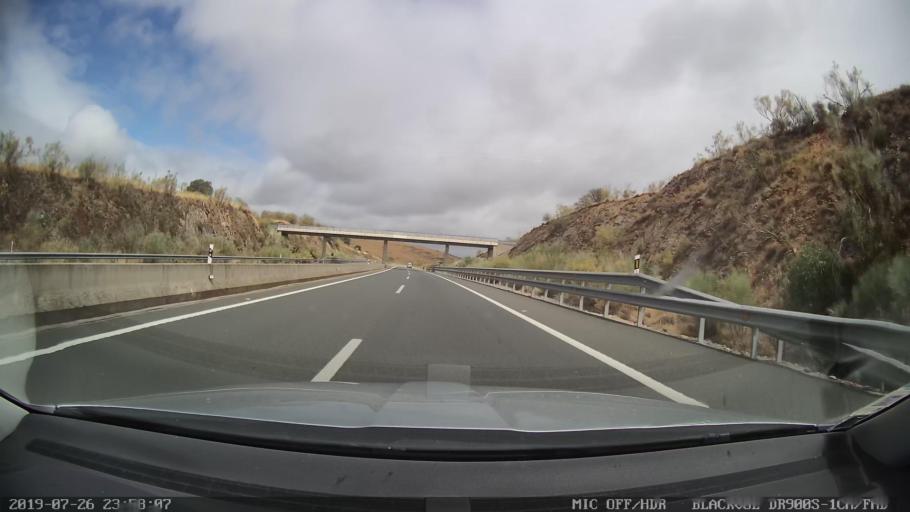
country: ES
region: Extremadura
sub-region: Provincia de Caceres
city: Romangordo
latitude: 39.7432
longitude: -5.7253
